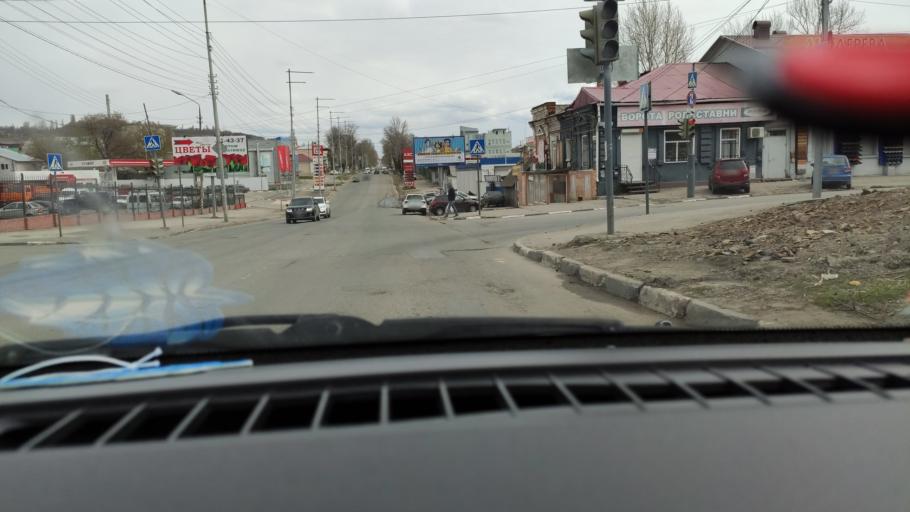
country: RU
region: Saratov
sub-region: Saratovskiy Rayon
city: Saratov
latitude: 51.5437
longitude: 46.0346
